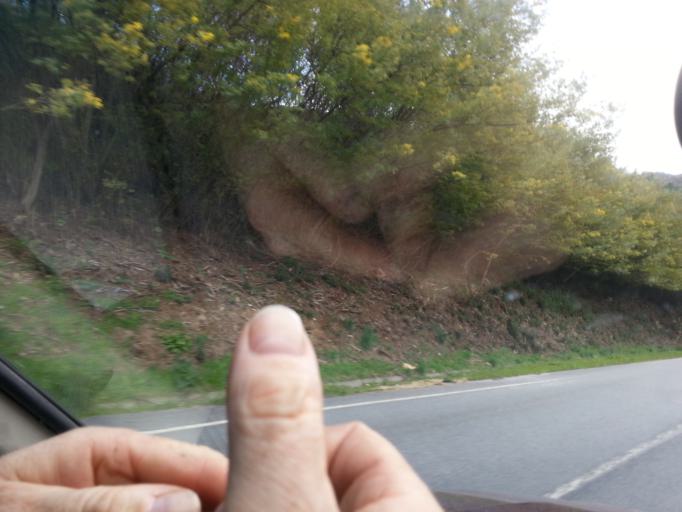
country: PT
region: Guarda
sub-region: Guarda
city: Guarda
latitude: 40.5596
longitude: -7.3009
